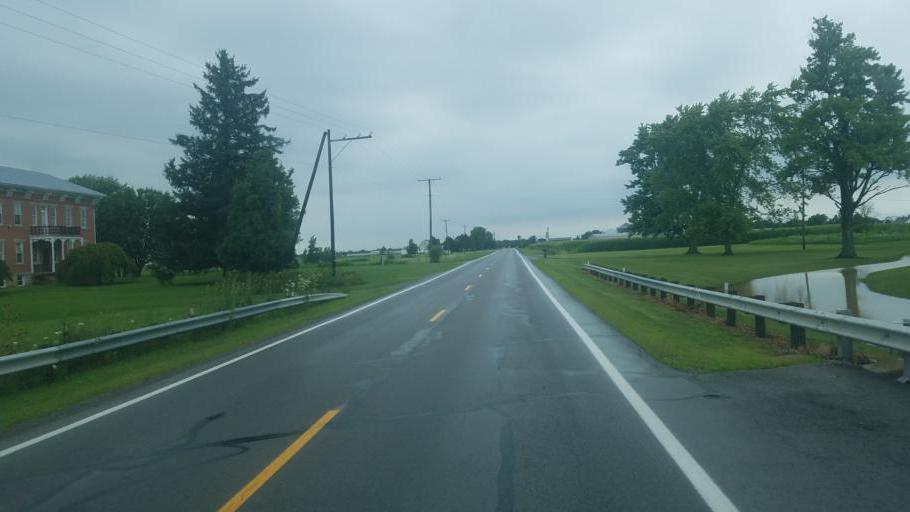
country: US
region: Ohio
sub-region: Hardin County
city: Kenton
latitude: 40.6193
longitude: -83.5970
